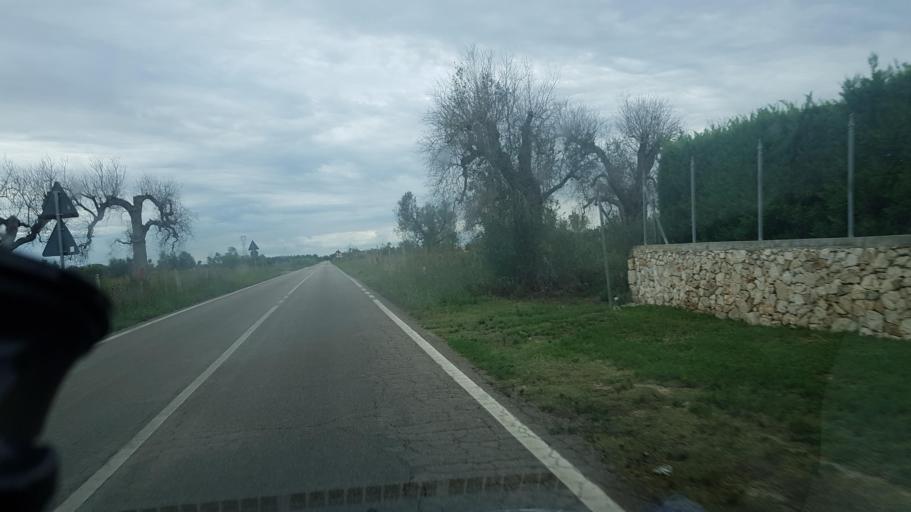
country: IT
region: Apulia
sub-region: Provincia di Lecce
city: Campi Salentina
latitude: 40.3640
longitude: 18.0063
